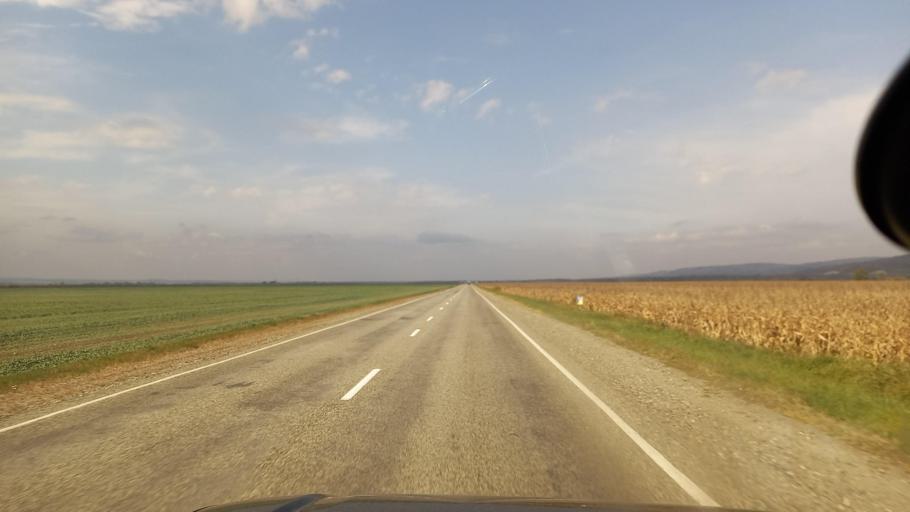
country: RU
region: Krasnodarskiy
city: Perepravnaya
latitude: 44.3034
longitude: 40.8604
